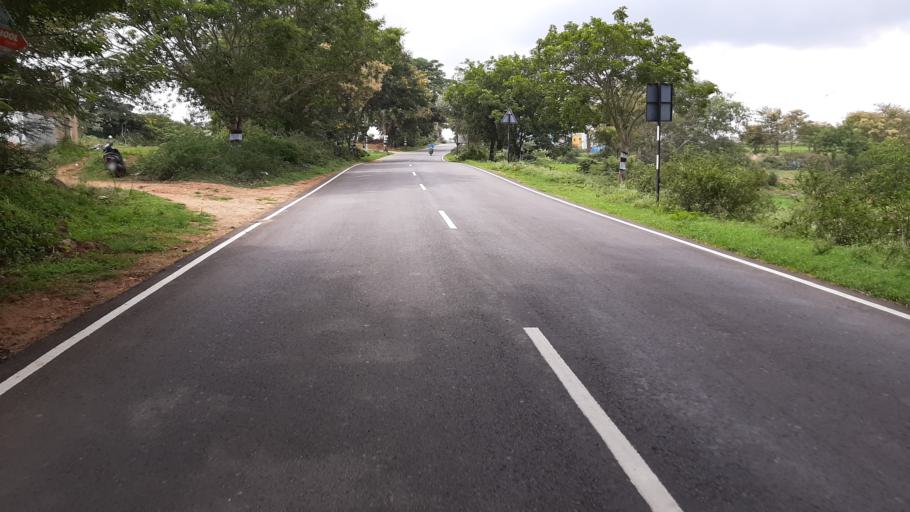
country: IN
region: Tamil Nadu
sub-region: Krishnagiri
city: Denkanikota
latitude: 12.5371
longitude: 77.7705
